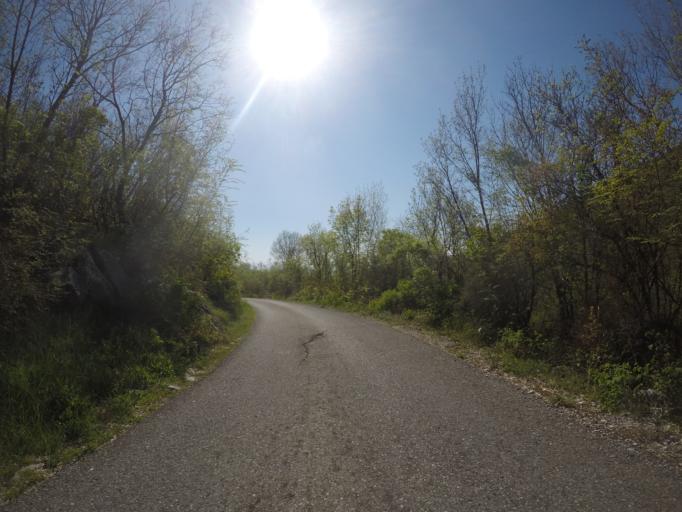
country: ME
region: Danilovgrad
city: Danilovgrad
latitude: 42.5139
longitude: 19.0677
